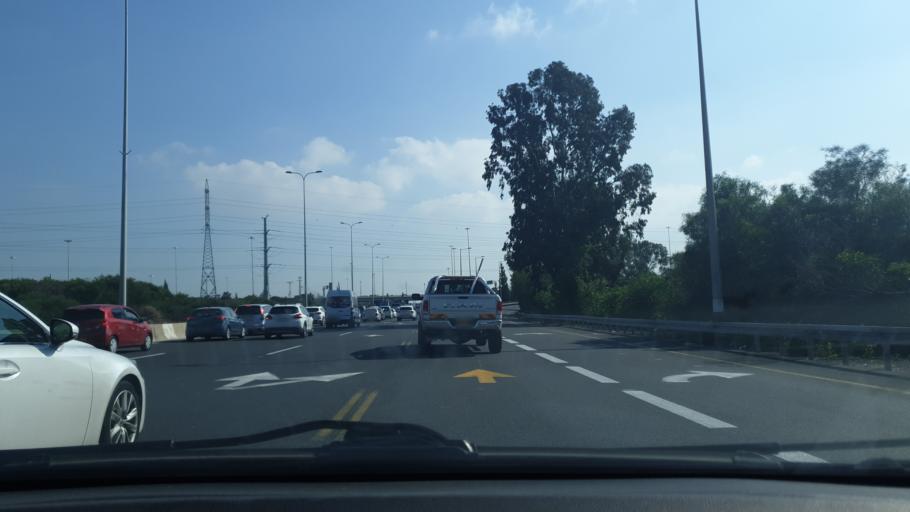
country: IL
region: Tel Aviv
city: Azor
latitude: 32.0138
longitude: 34.8119
